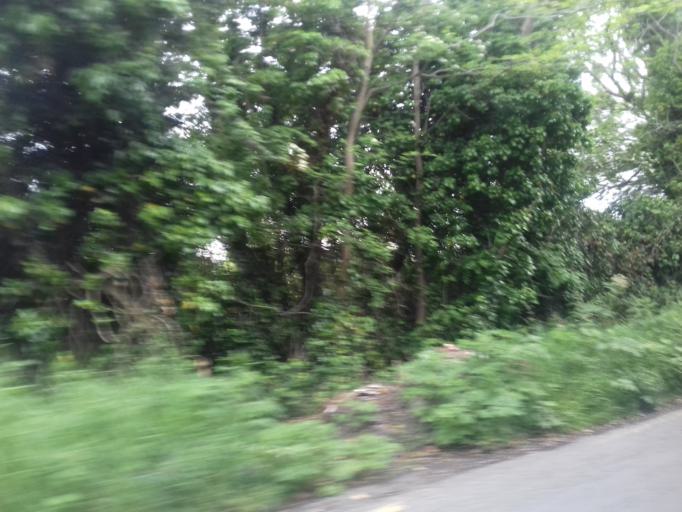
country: IE
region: Leinster
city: Donabate
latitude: 53.4935
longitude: -6.1874
